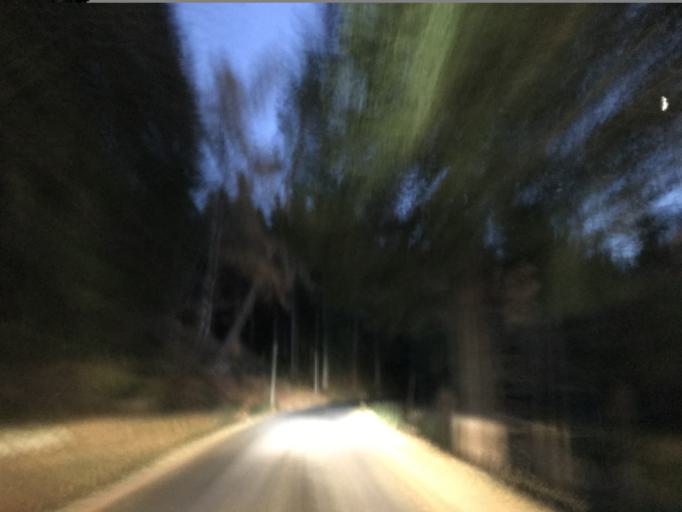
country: FR
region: Rhone-Alpes
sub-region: Departement de la Loire
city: Noiretable
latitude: 45.7474
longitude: 3.7087
